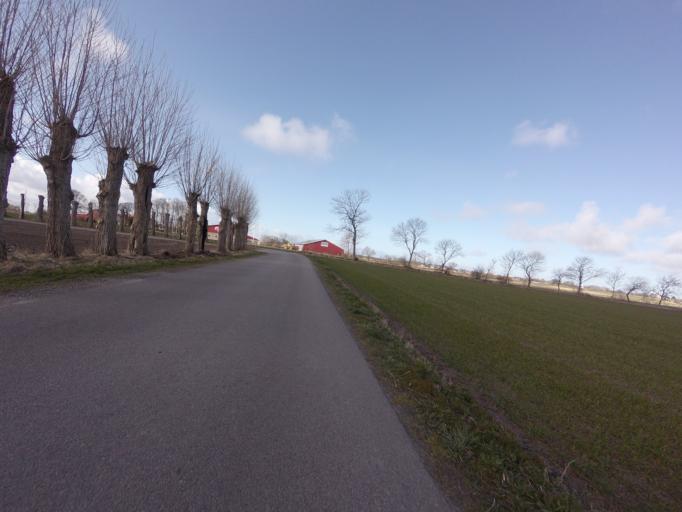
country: SE
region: Skane
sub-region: Hoganas Kommun
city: Hoganas
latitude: 56.1872
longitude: 12.6209
